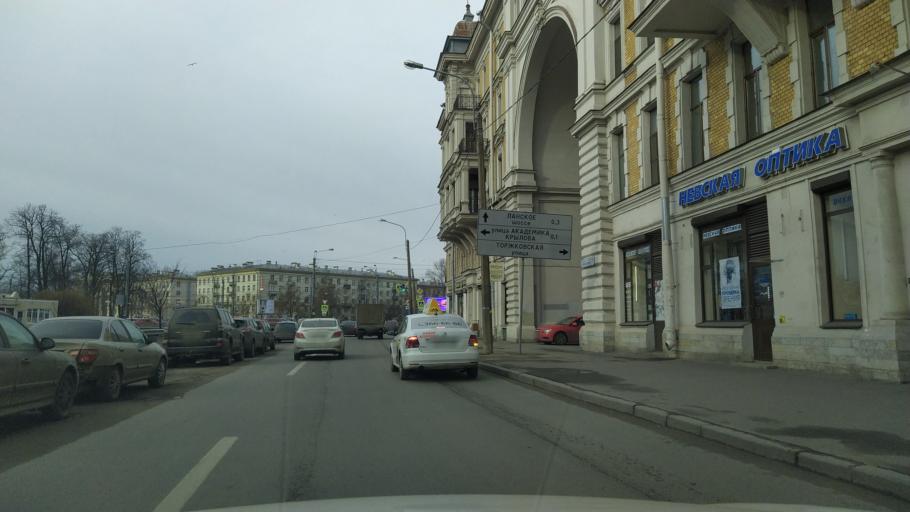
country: RU
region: Leningrad
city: Chernaya Rechka
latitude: 59.9858
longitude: 30.3046
